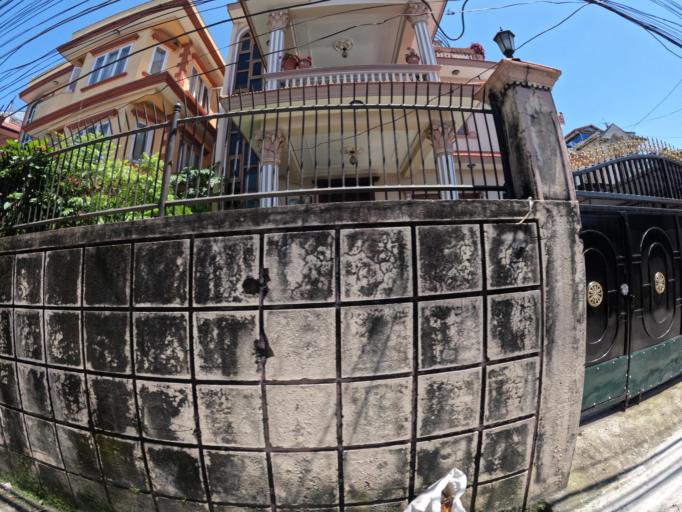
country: NP
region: Central Region
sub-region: Bagmati Zone
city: Kathmandu
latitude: 27.7476
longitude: 85.3264
